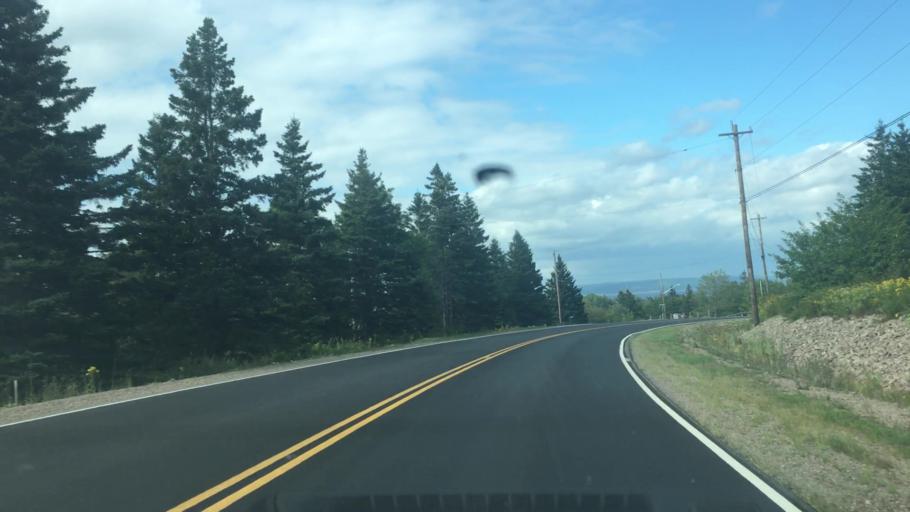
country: CA
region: Nova Scotia
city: Princeville
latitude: 45.7894
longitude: -60.7406
